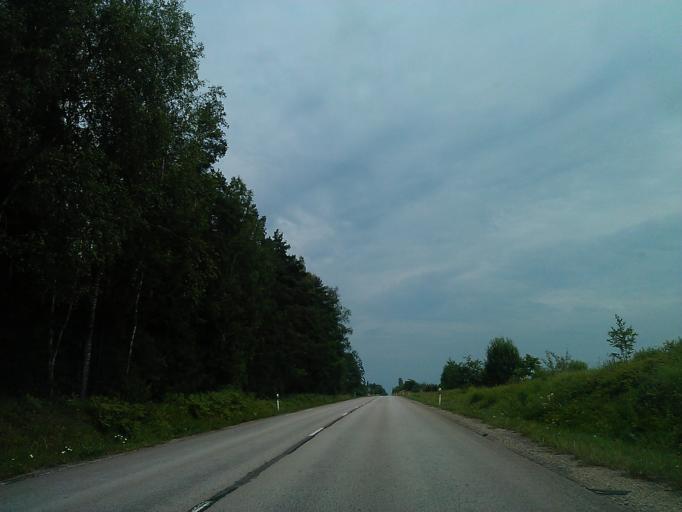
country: LV
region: Valmieras Rajons
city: Valmiera
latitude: 57.4753
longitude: 25.4058
